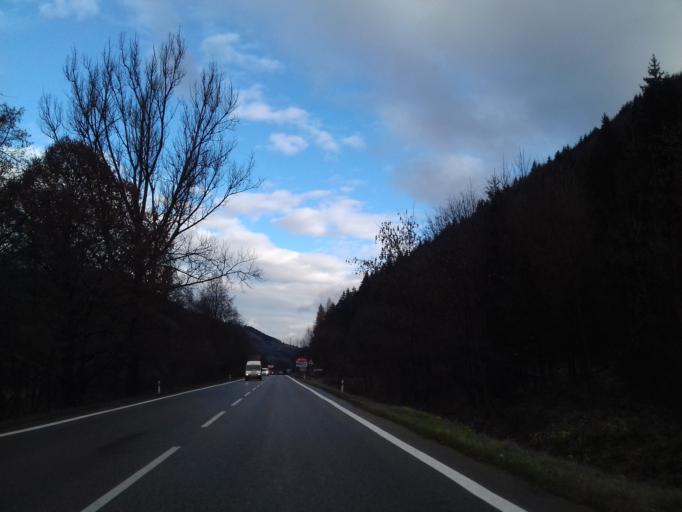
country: SK
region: Zilinsky
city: Ruzomberok
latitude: 49.0195
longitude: 19.2925
